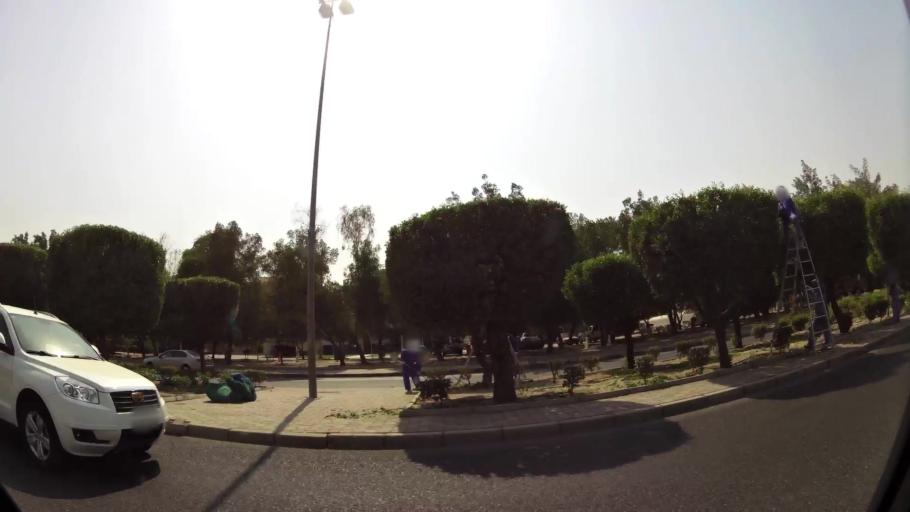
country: KW
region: Al Asimah
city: Ash Shamiyah
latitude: 29.3333
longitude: 47.9587
